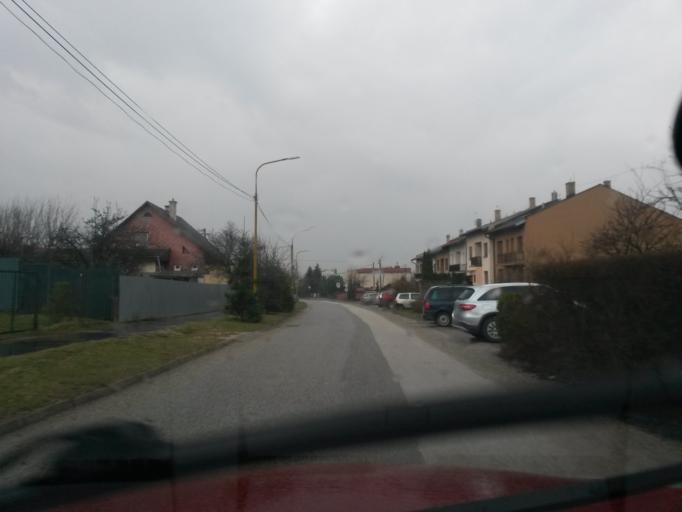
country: SK
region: Kosicky
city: Kosice
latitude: 48.7392
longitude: 21.2908
